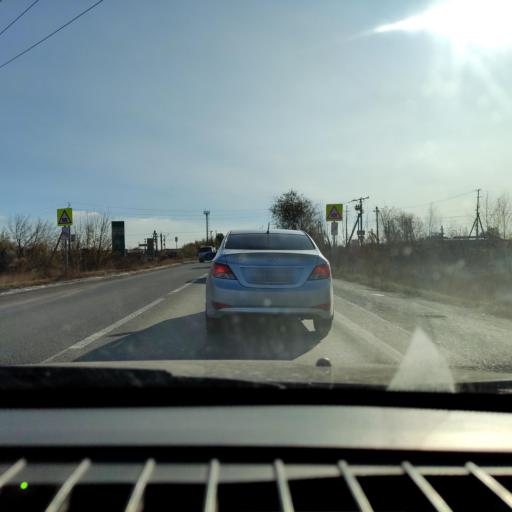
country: RU
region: Samara
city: Tol'yatti
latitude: 53.5629
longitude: 49.3546
